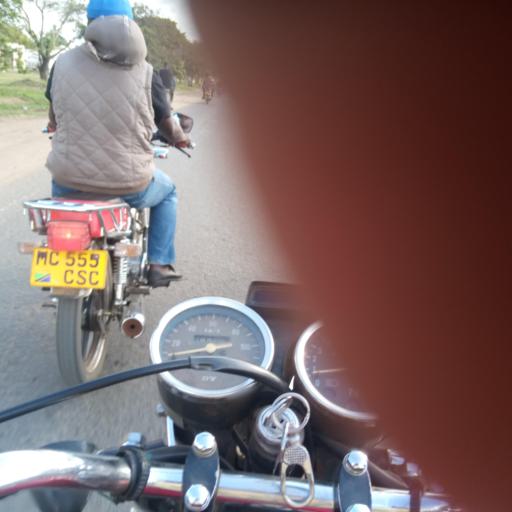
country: TZ
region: Tanga
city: Tanga
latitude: -5.0932
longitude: 39.0961
